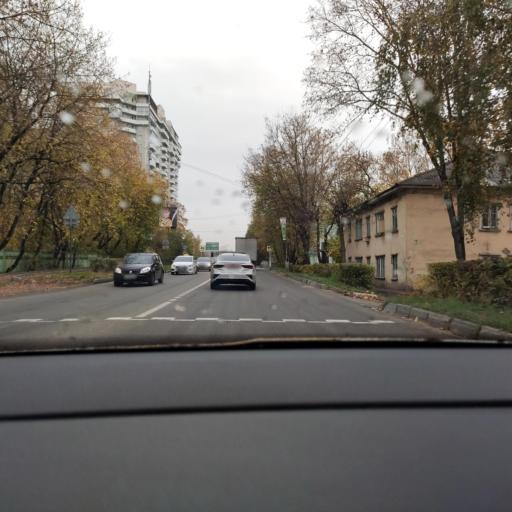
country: RU
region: Moskovskaya
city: Ivanteyevka
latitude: 55.9674
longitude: 37.9012
